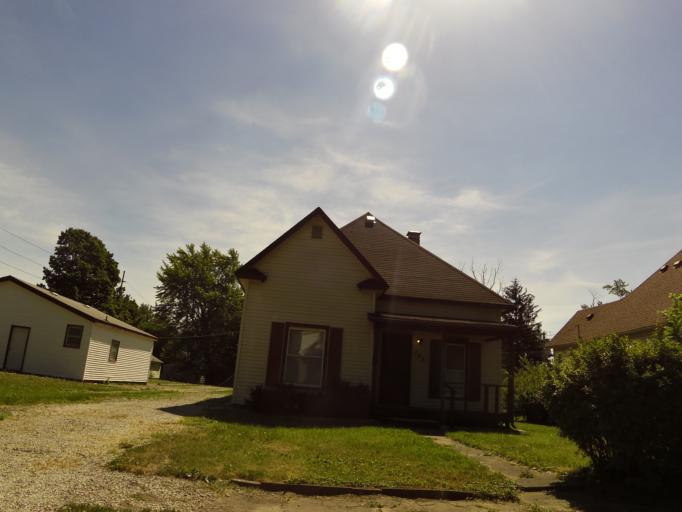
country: US
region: Illinois
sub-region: Vermilion County
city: Danville
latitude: 40.1346
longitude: -87.5845
